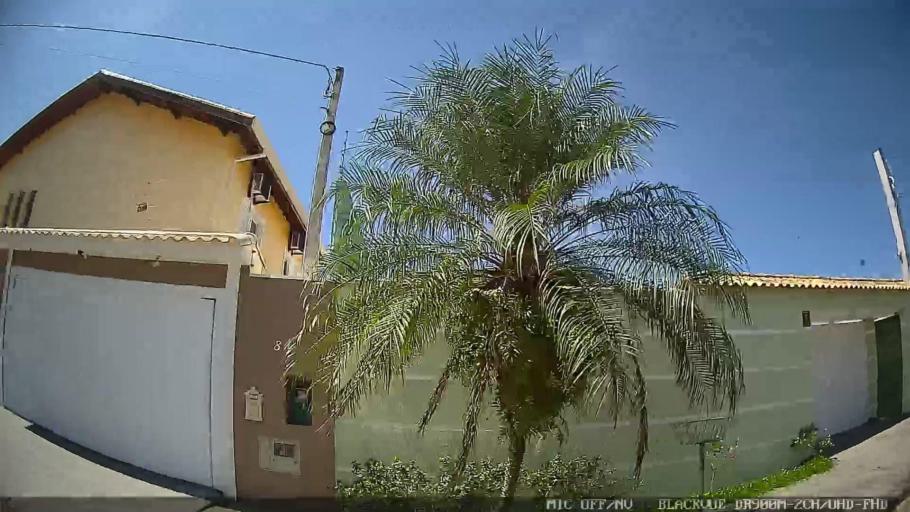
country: BR
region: Sao Paulo
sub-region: Peruibe
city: Peruibe
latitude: -24.3045
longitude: -46.9817
